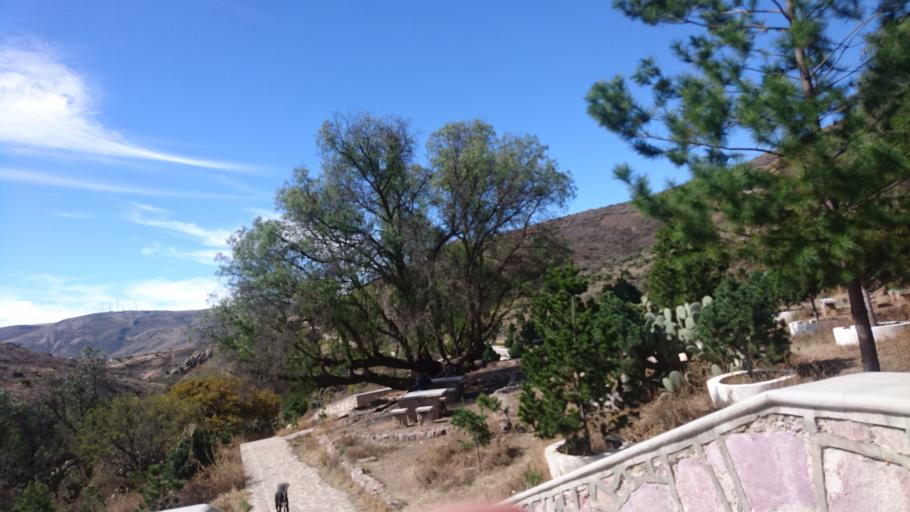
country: MX
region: Zacatecas
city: Guadalupe
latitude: 22.7799
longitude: -102.5441
